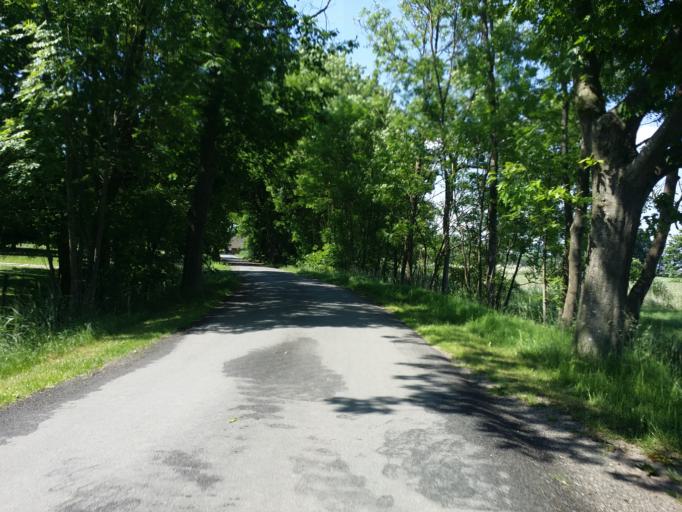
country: DE
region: Lower Saxony
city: Neuenkirchen
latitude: 53.1640
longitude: 8.5128
